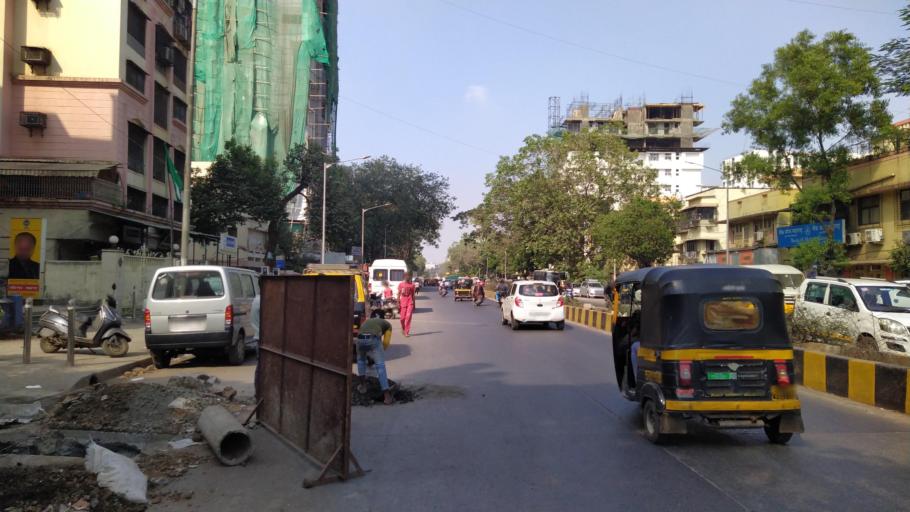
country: IN
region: Maharashtra
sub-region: Mumbai Suburban
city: Mumbai
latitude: 19.0665
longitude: 72.8748
